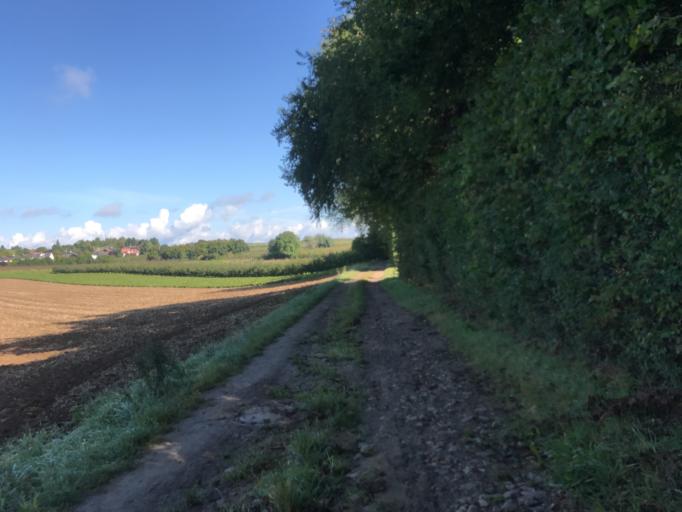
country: DE
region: Rheinland-Pfalz
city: Klein-Winternheim
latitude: 49.9698
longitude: 8.2009
